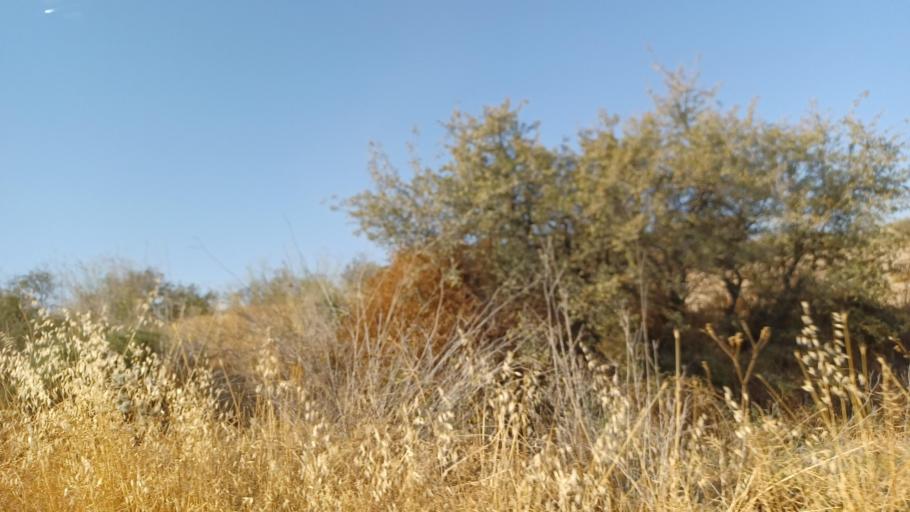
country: CY
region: Pafos
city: Polis
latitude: 35.0197
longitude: 32.4245
